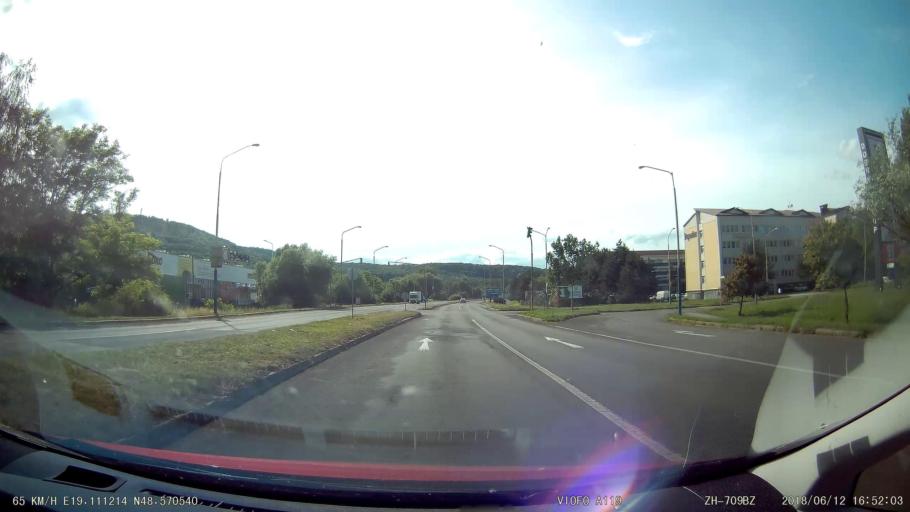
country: SK
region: Banskobystricky
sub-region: Okres Banska Bystrica
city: Zvolen
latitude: 48.5707
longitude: 19.1107
